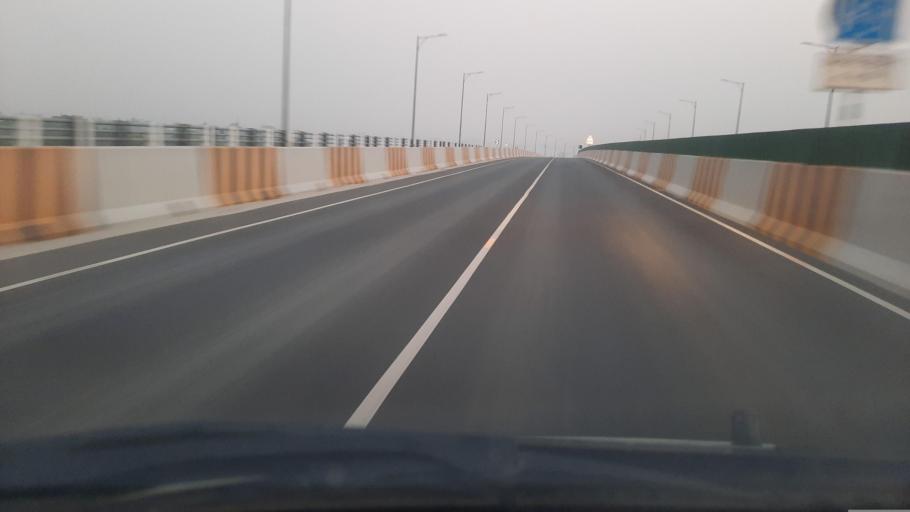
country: BD
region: Dhaka
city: Dohar
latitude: 23.5157
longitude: 90.2787
